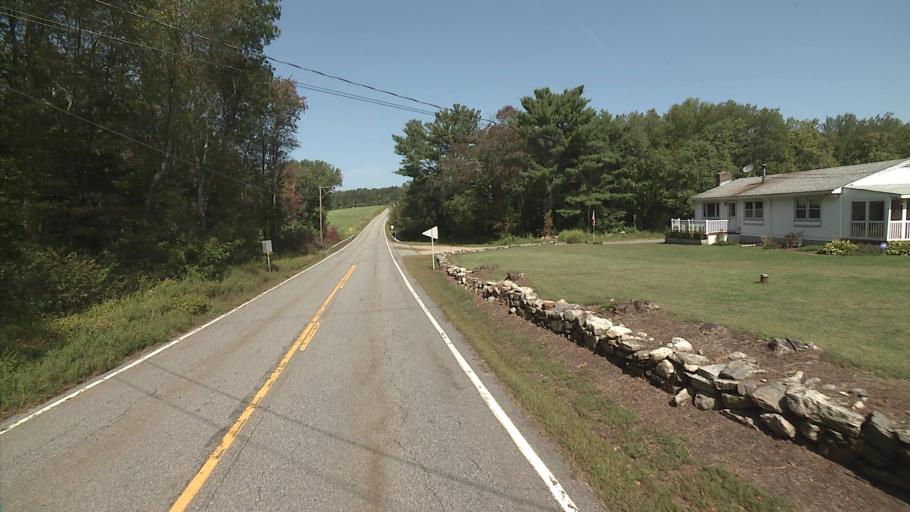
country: US
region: Connecticut
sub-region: Windham County
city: Quinebaug
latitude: 42.0133
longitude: -72.0036
